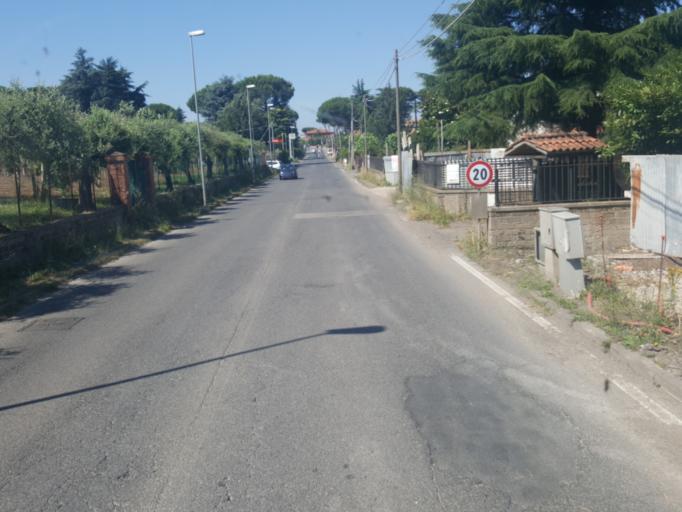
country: IT
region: Latium
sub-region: Citta metropolitana di Roma Capitale
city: Frascati
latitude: 41.8272
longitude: 12.6483
